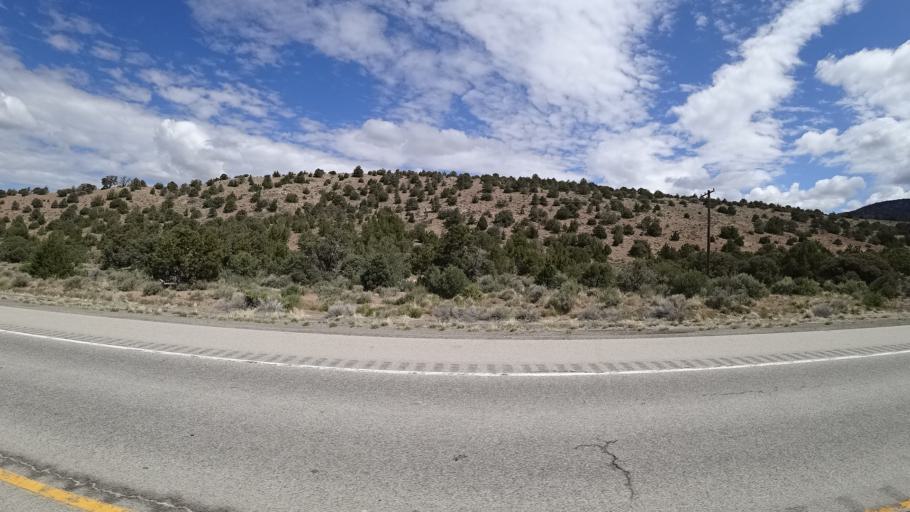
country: US
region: Nevada
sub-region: Douglas County
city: Gardnerville Ranchos
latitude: 38.8529
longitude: -119.6560
